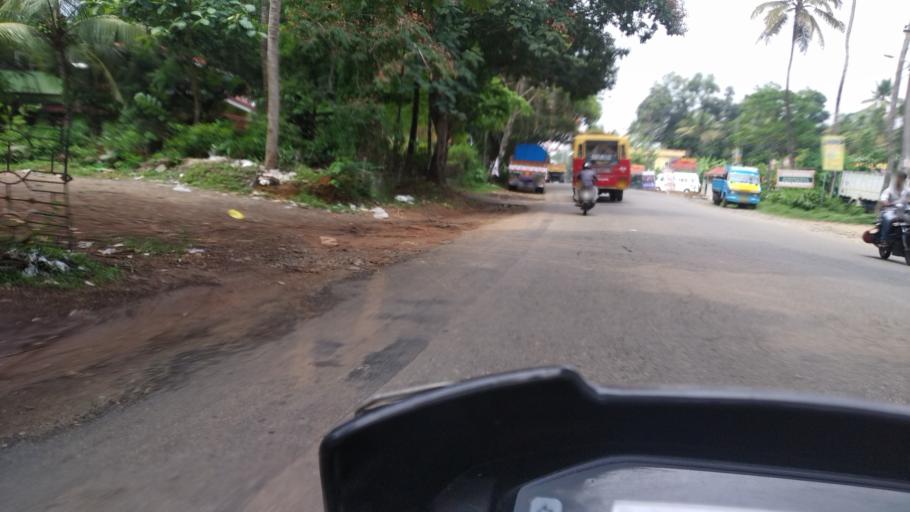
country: IN
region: Kerala
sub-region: Ernakulam
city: Kotamangalam
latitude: 10.0953
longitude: 76.5548
